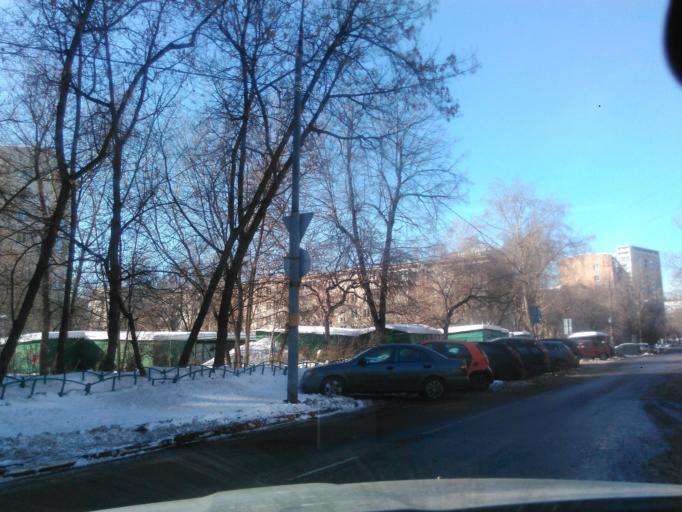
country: RU
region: Moskovskaya
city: Dorogomilovo
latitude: 55.7931
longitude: 37.5691
